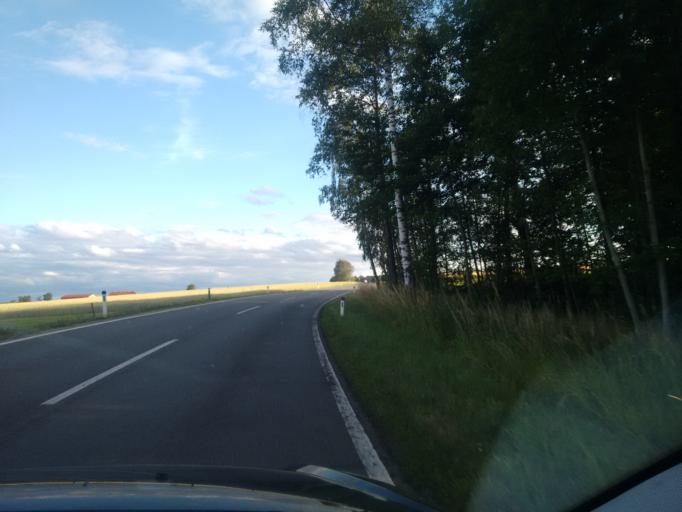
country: AT
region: Upper Austria
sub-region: Politischer Bezirk Urfahr-Umgebung
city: Gramastetten
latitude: 48.4034
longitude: 14.1823
